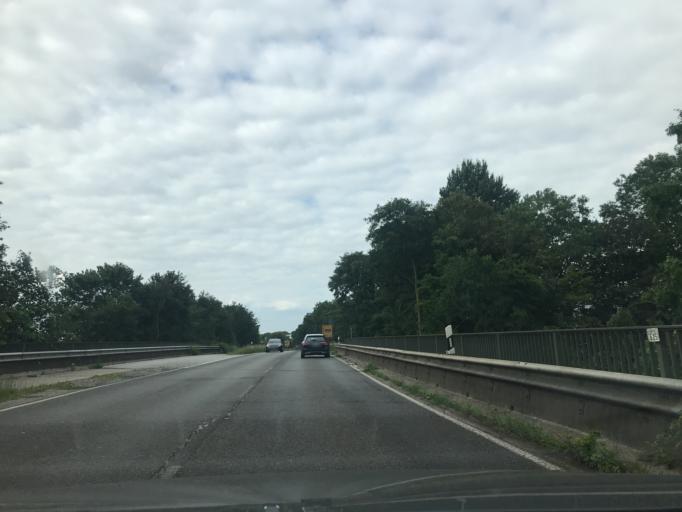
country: DE
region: North Rhine-Westphalia
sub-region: Regierungsbezirk Dusseldorf
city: Neuss
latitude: 51.1649
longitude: 6.7236
